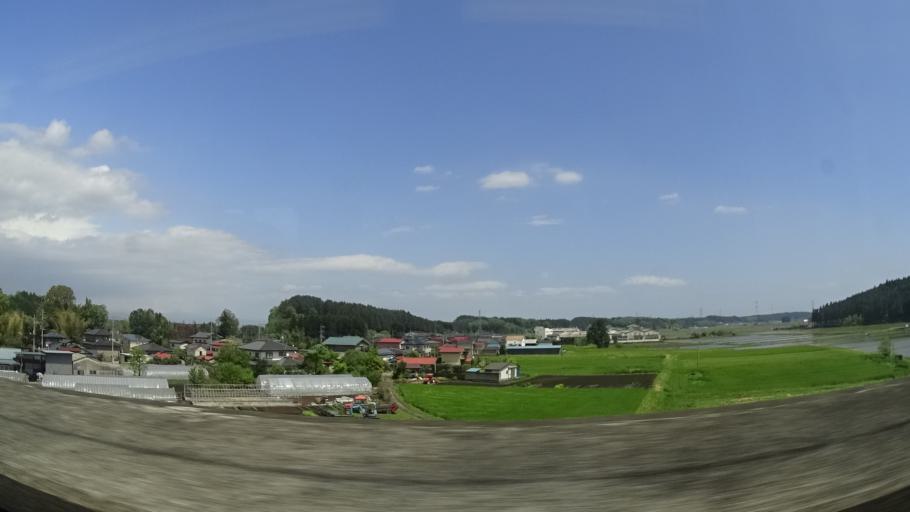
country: JP
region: Tochigi
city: Yaita
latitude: 36.8188
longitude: 139.9591
